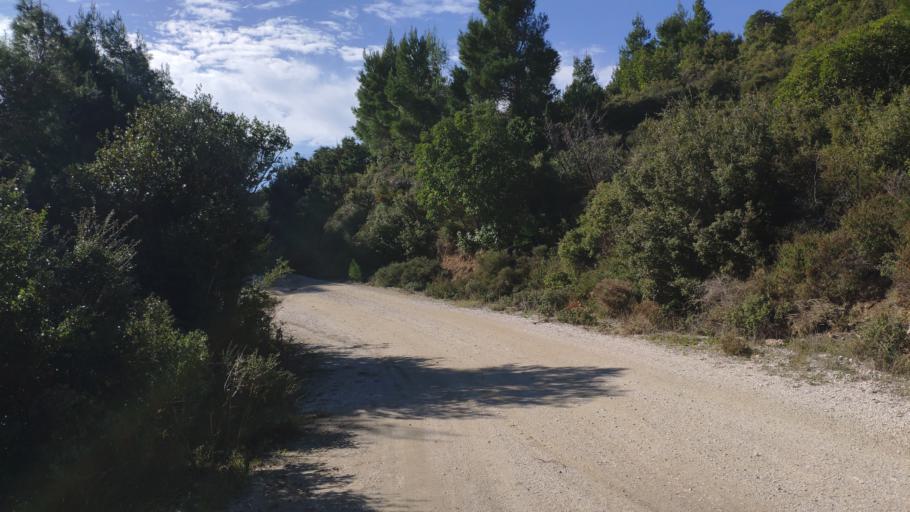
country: GR
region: Attica
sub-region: Nomarchia Anatolikis Attikis
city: Thrakomakedones
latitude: 38.1500
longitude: 23.7741
